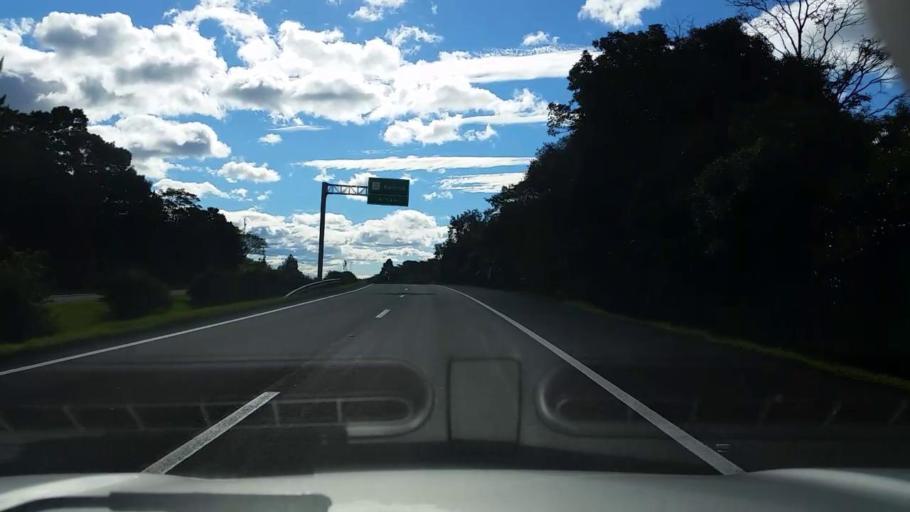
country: BR
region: Rio Grande do Sul
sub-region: Capao Da Canoa
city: Capao da Canoa
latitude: -29.6514
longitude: -50.1185
